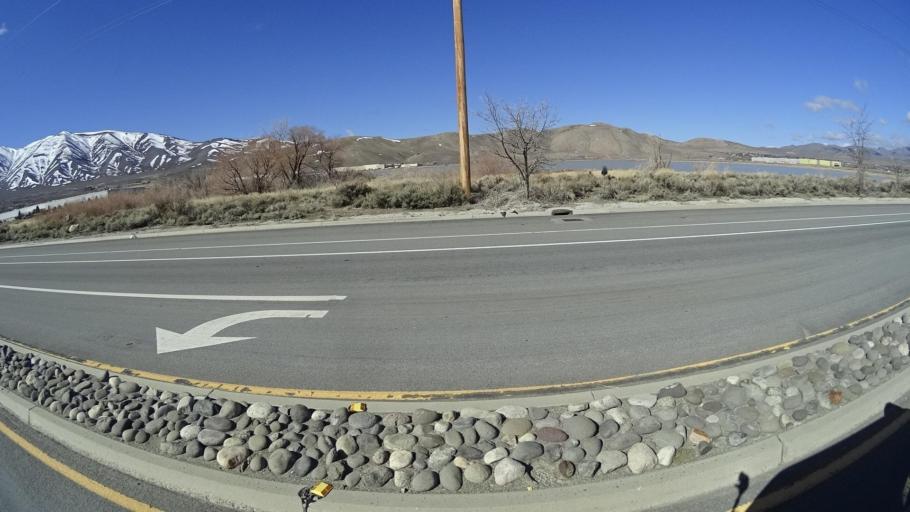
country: US
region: Nevada
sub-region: Washoe County
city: Lemmon Valley
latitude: 39.6403
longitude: -119.8969
